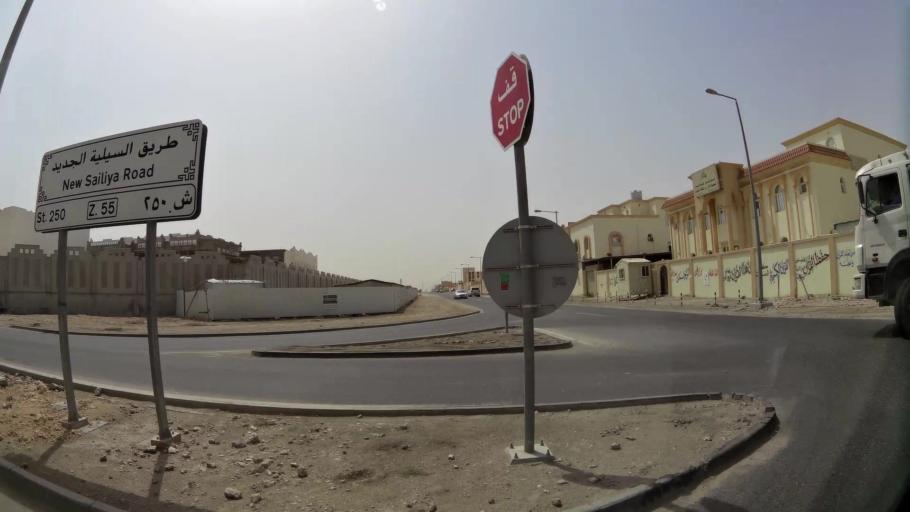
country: QA
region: Baladiyat ar Rayyan
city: Ar Rayyan
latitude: 25.2503
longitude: 51.3761
